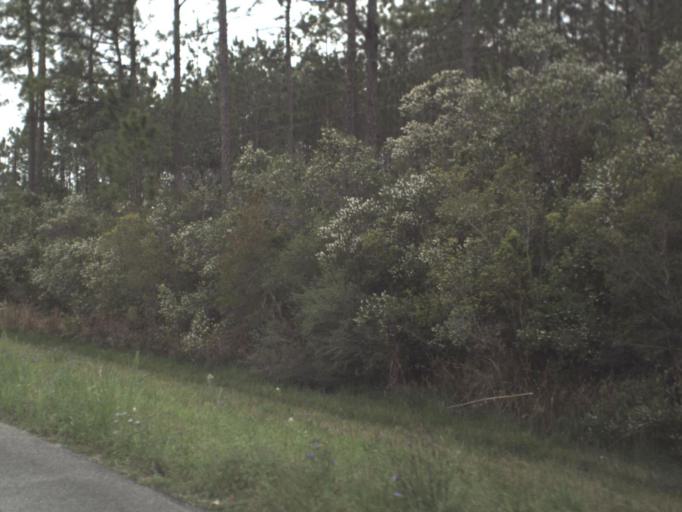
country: US
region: Florida
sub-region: Gulf County
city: Port Saint Joe
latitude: 29.8981
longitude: -85.2122
